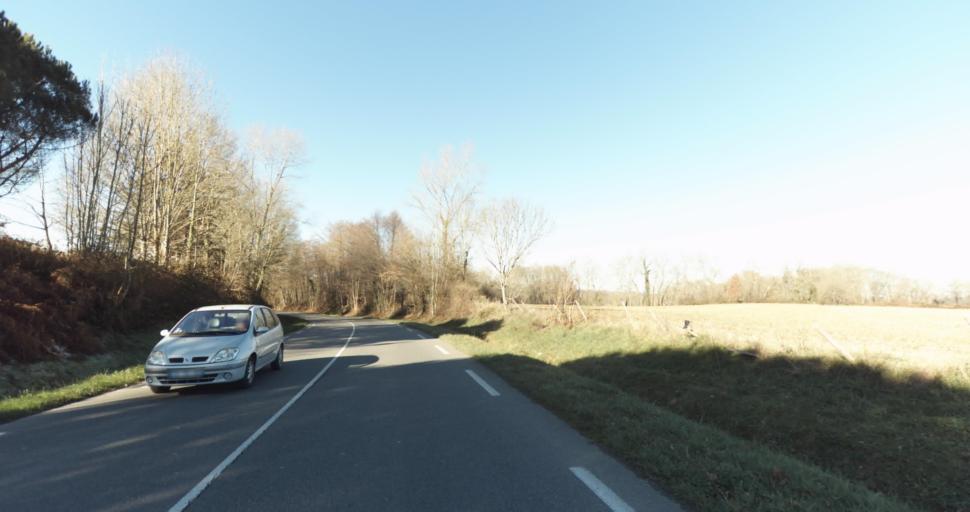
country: FR
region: Aquitaine
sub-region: Departement des Pyrenees-Atlantiques
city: Morlaas
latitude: 43.3518
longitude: -0.2587
